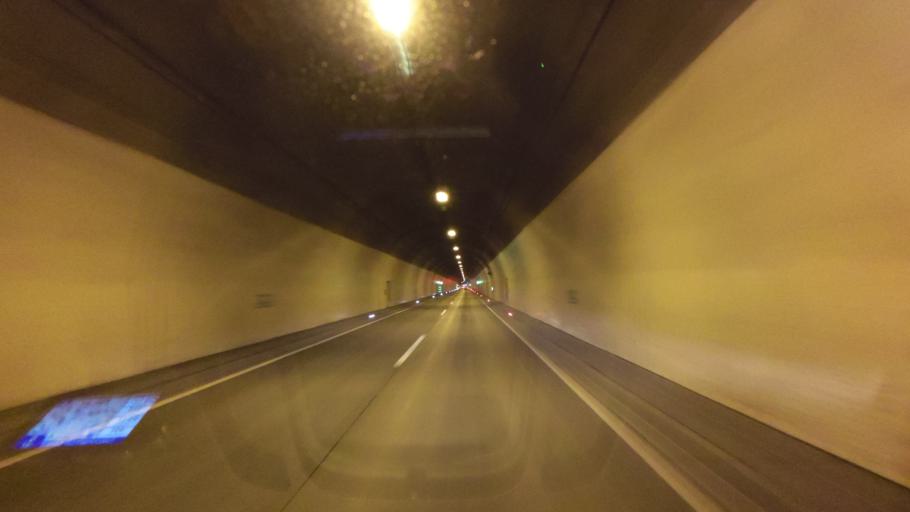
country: AT
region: Salzburg
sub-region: Politischer Bezirk Hallein
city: Golling an der Salzach
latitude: 47.5527
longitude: 13.1745
